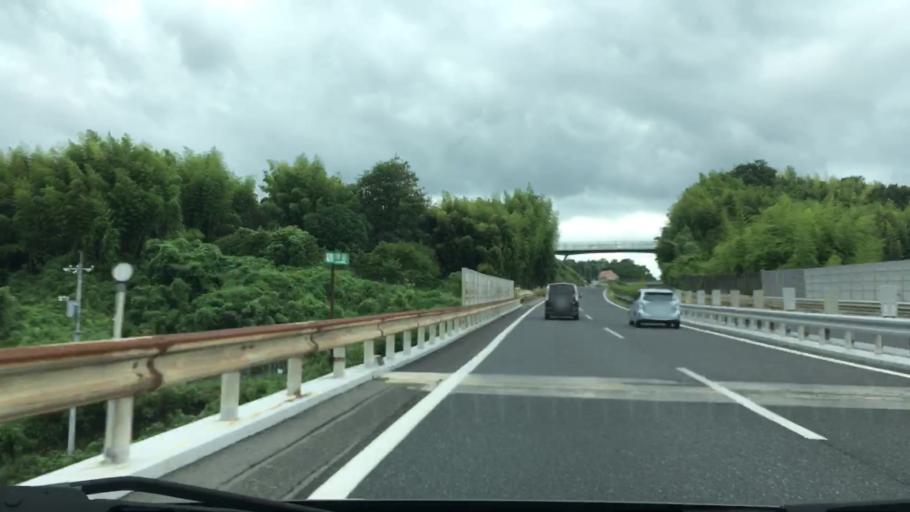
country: JP
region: Okayama
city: Tsuyama
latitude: 35.0710
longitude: 134.0287
